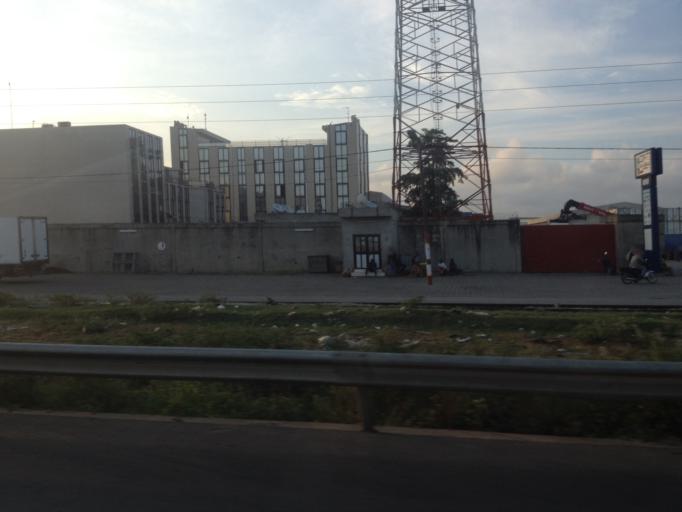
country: BJ
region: Queme
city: Porto-Novo
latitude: 6.3763
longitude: 2.5793
